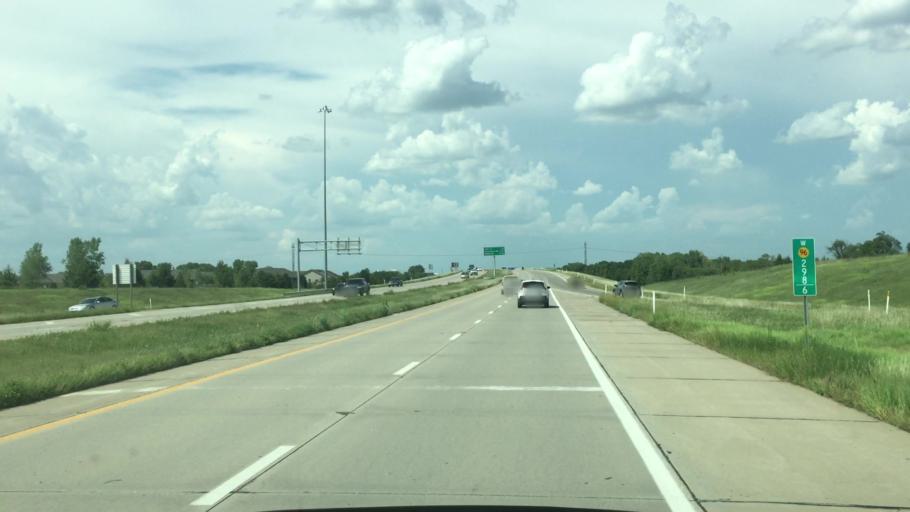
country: US
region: Kansas
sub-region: Butler County
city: Andover
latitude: 37.7108
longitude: -97.2000
